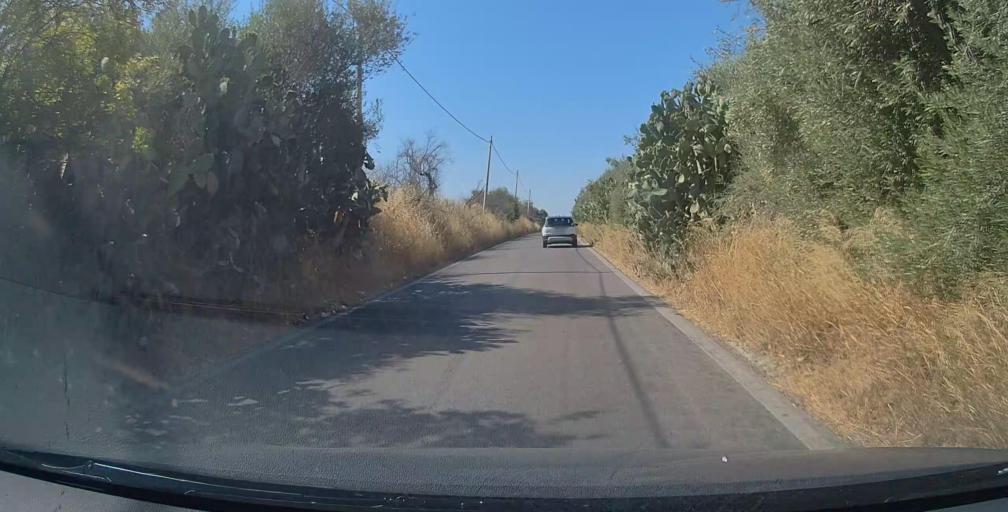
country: IT
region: Sicily
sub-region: Catania
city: Palazzolo
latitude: 37.5435
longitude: 14.9301
